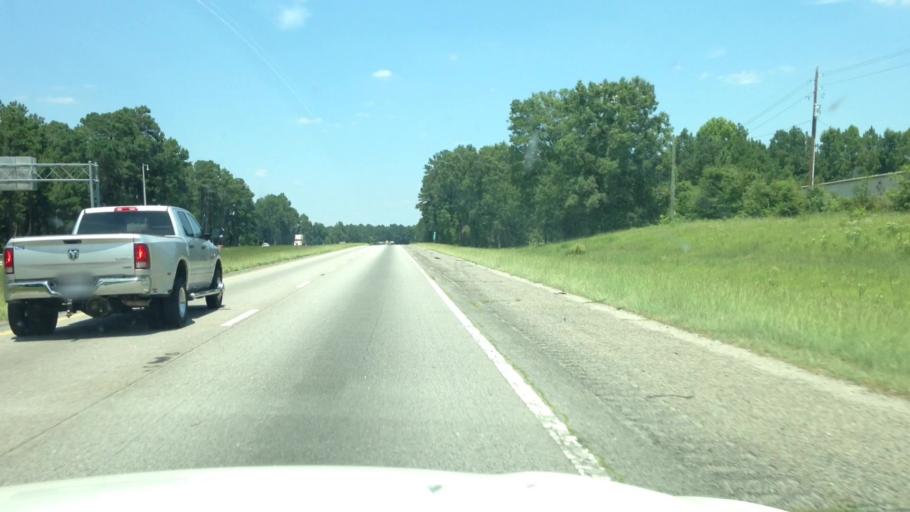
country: US
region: North Carolina
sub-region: Robeson County
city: Rowland
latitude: 34.4865
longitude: -79.3330
